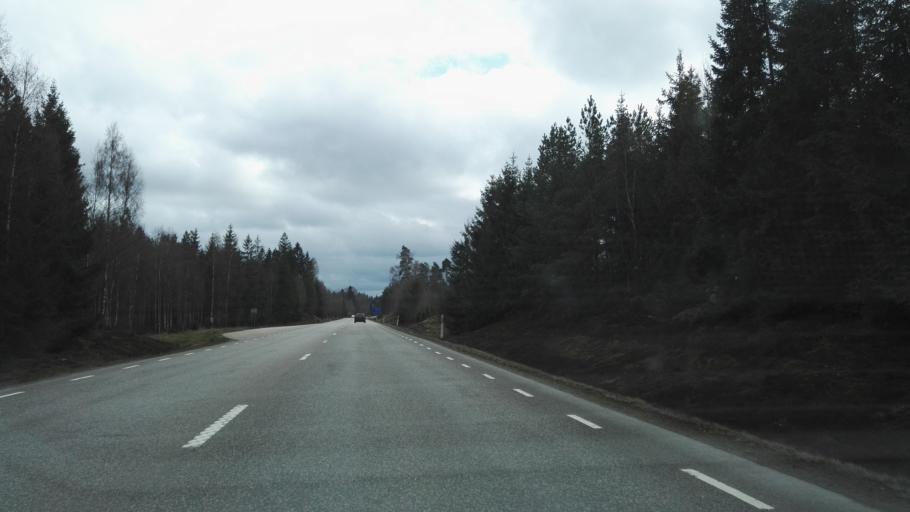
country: SE
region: Kronoberg
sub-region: Almhults Kommun
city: AElmhult
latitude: 56.5695
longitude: 14.1839
